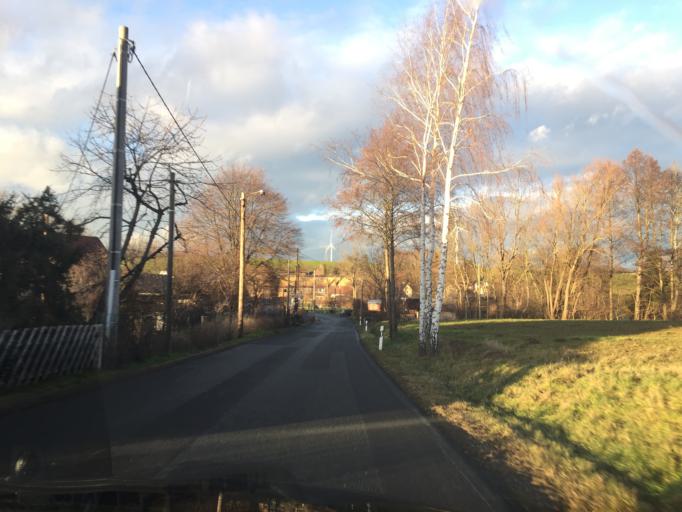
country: DE
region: Thuringia
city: Nobdenitz
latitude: 50.8842
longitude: 12.3069
